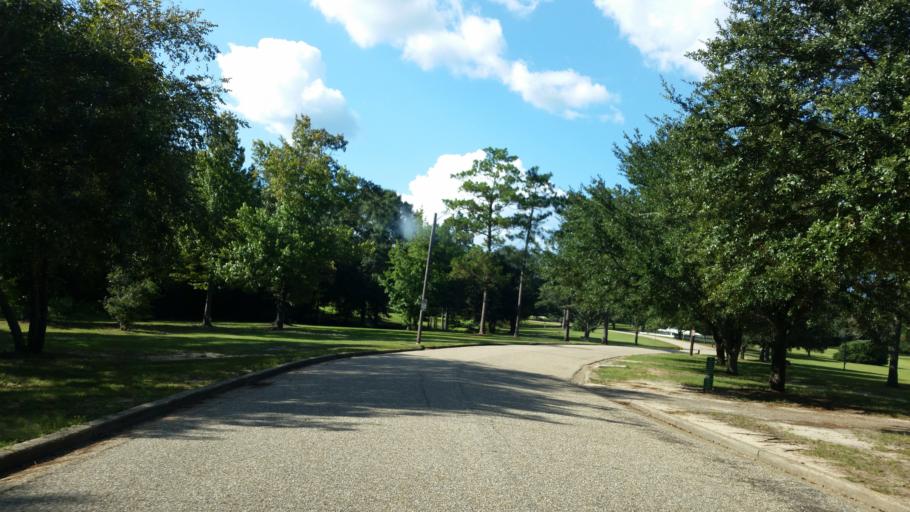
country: US
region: Alabama
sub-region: Mobile County
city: Prichard
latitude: 30.7073
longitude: -88.1615
